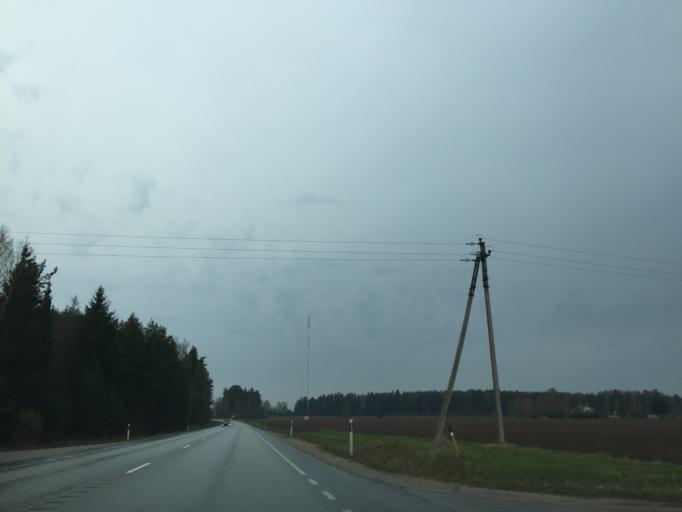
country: EE
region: Tartu
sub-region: UElenurme vald
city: Ulenurme
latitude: 58.2222
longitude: 26.7016
